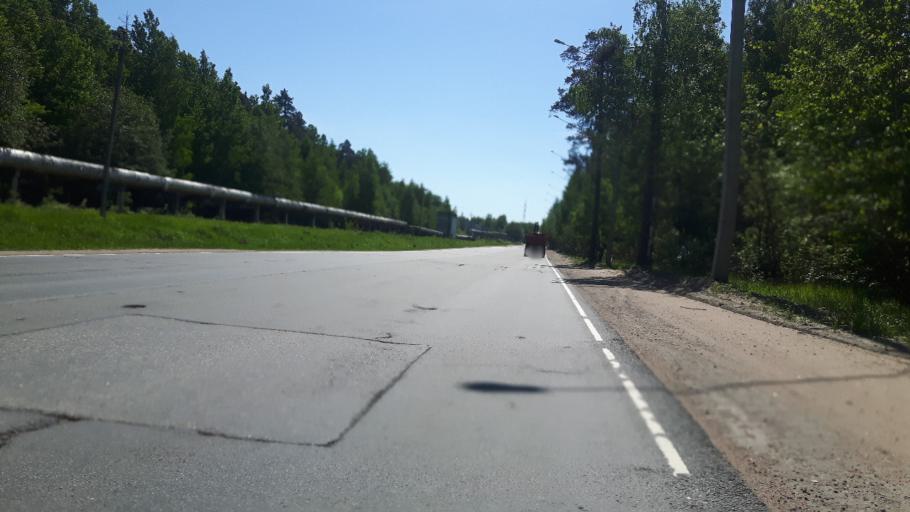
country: RU
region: Leningrad
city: Sosnovyy Bor
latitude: 59.8633
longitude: 29.0670
